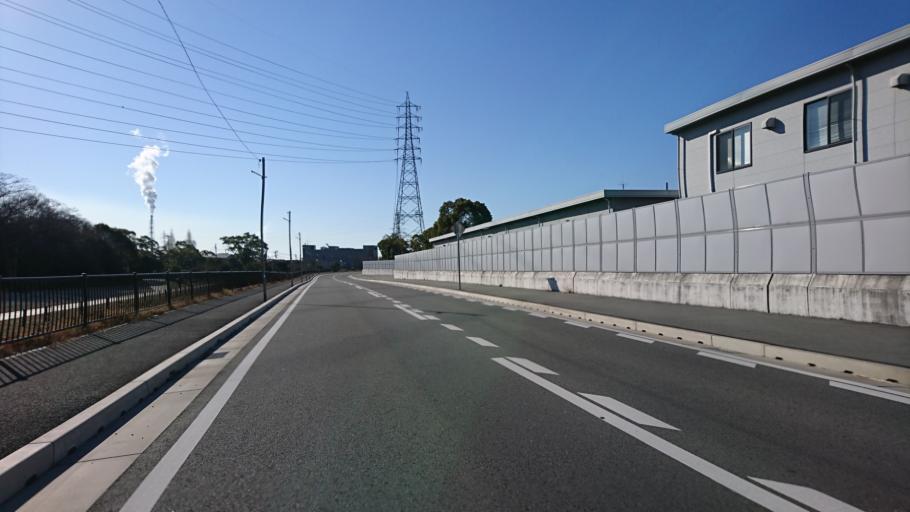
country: JP
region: Hyogo
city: Kakogawacho-honmachi
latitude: 34.7516
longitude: 134.7916
